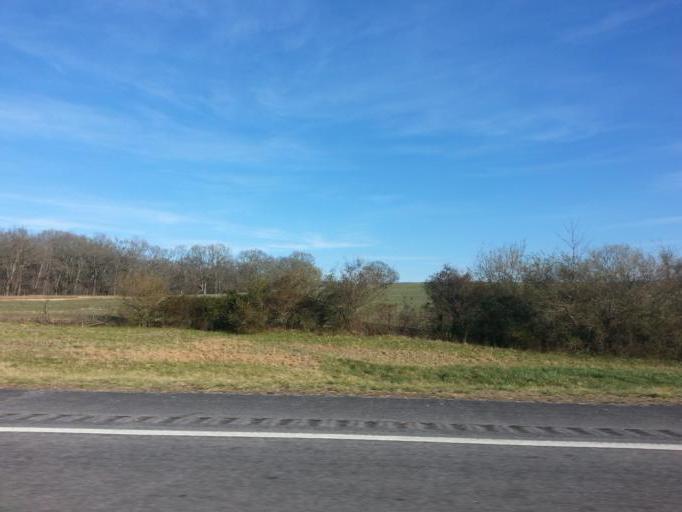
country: US
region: Tennessee
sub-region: Warren County
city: McMinnville
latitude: 35.7261
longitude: -85.6697
